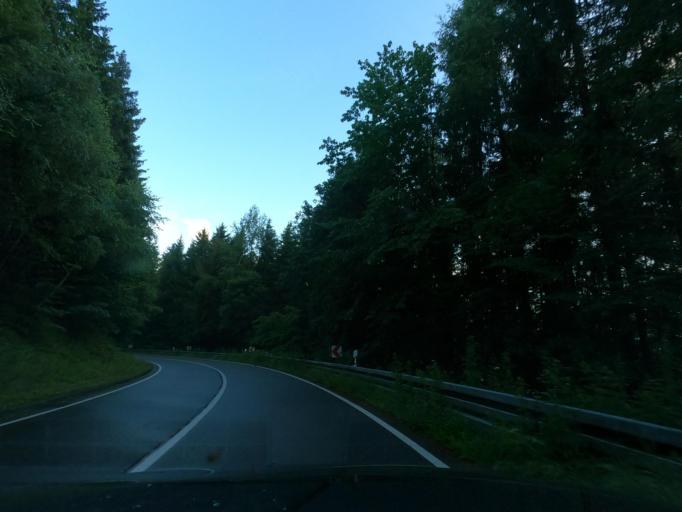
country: DE
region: North Rhine-Westphalia
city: Plettenberg
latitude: 51.2482
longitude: 7.9136
